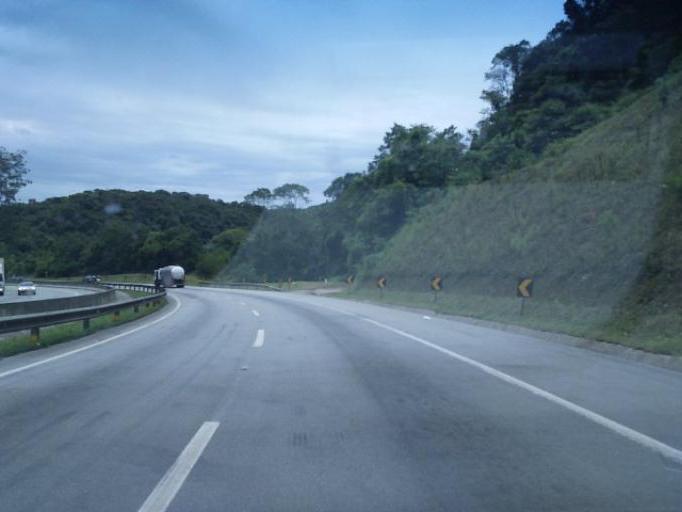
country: BR
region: Sao Paulo
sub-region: Juquitiba
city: Juquitiba
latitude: -24.0381
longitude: -47.1919
